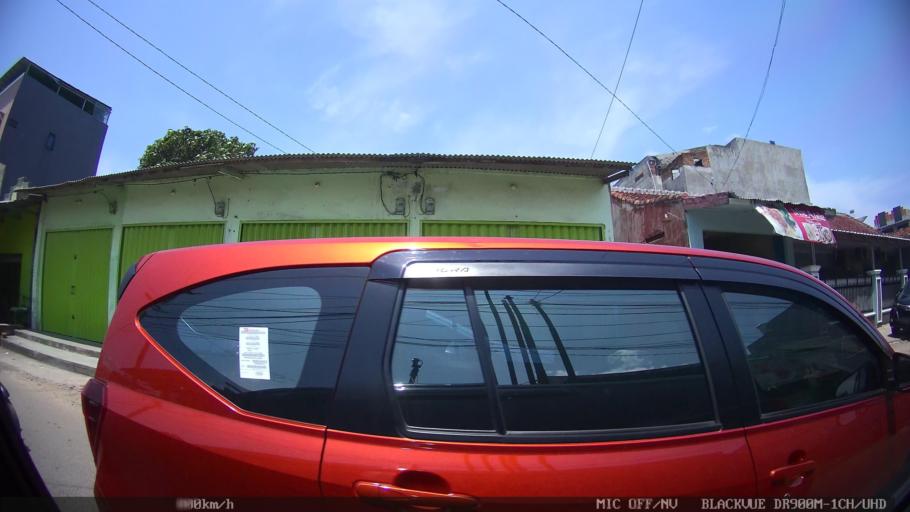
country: ID
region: Lampung
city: Bandarlampung
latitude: -5.4080
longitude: 105.2697
